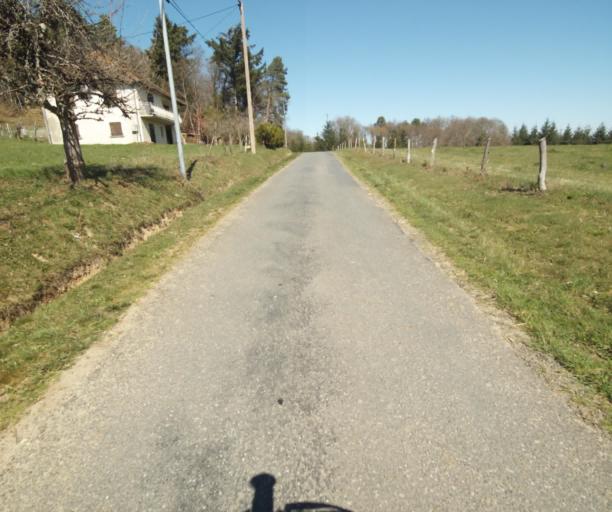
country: FR
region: Limousin
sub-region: Departement de la Correze
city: Saint-Mexant
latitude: 45.2883
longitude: 1.6416
